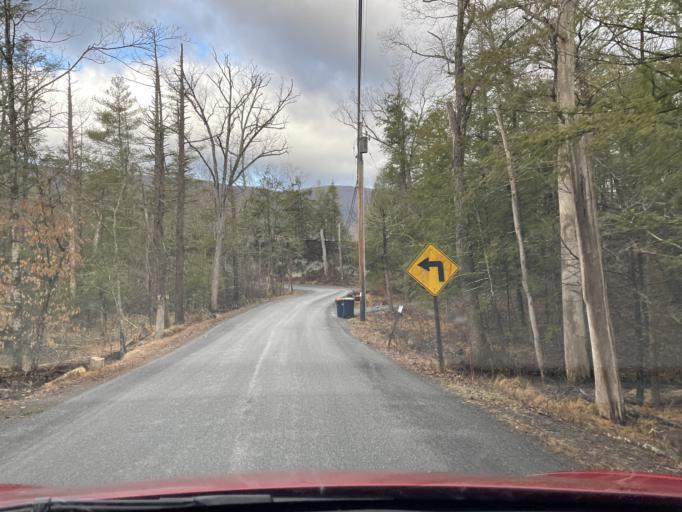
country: US
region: New York
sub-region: Ulster County
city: Manorville
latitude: 42.0840
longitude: -74.0447
